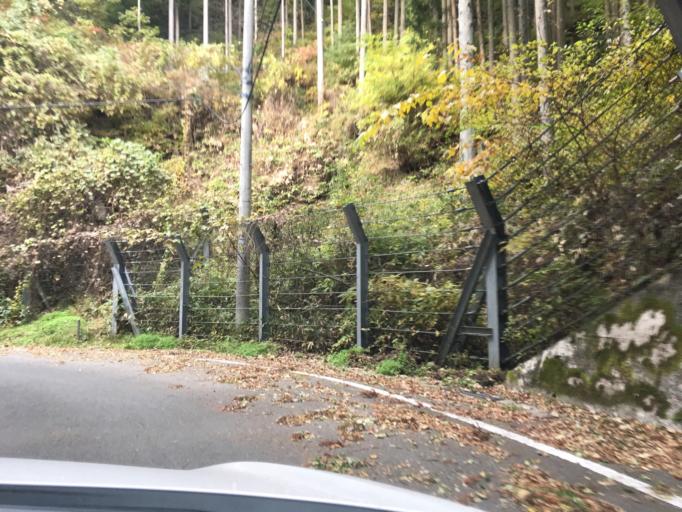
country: JP
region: Fukushima
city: Iwaki
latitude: 37.0971
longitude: 140.7902
